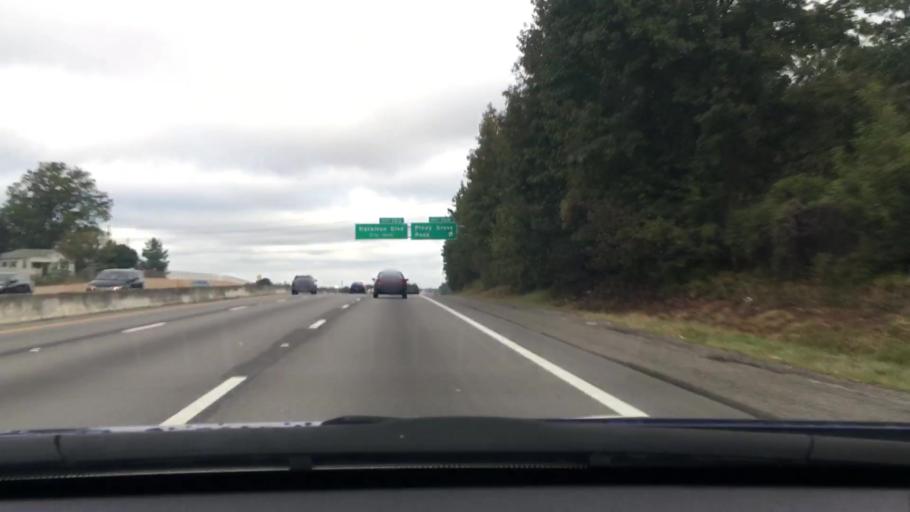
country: US
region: South Carolina
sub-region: Lexington County
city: Seven Oaks
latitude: 34.0631
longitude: -81.1377
